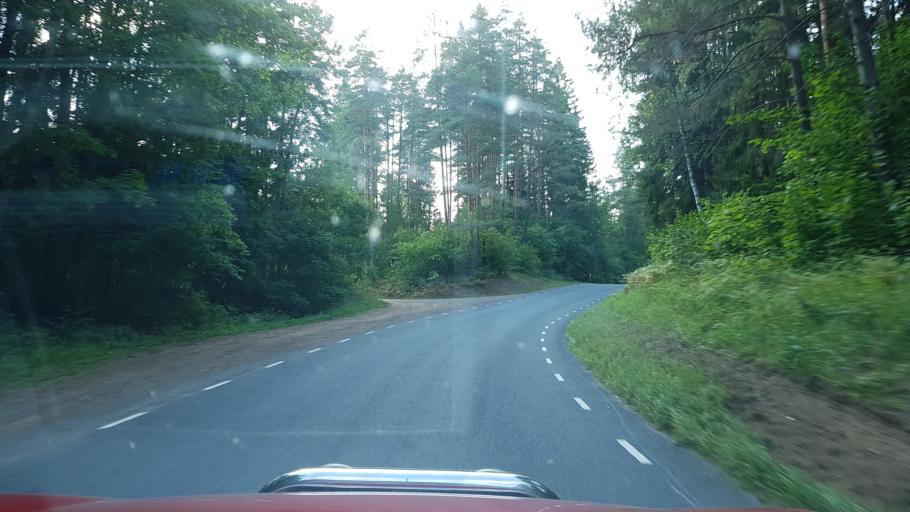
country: EE
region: Polvamaa
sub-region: Polva linn
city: Polva
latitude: 58.1516
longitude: 26.8730
